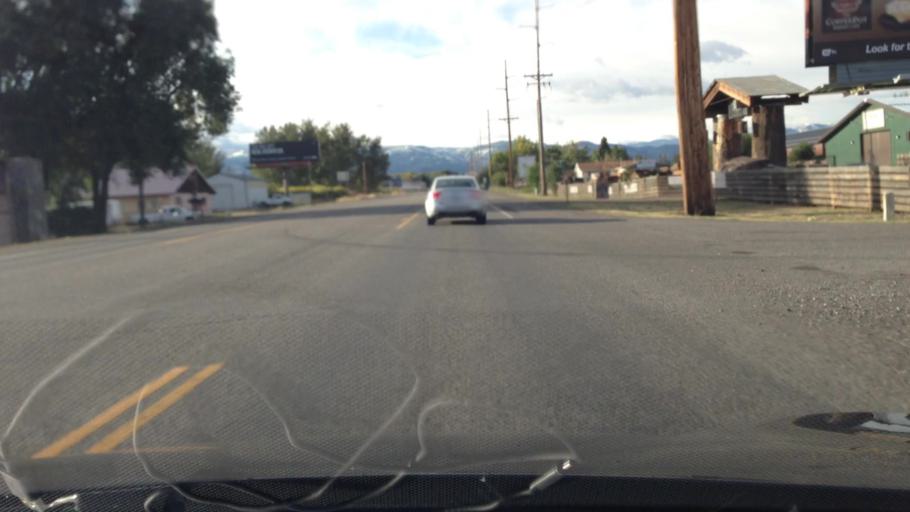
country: US
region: Montana
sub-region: Gallatin County
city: Four Corners
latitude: 45.6677
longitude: -111.1857
